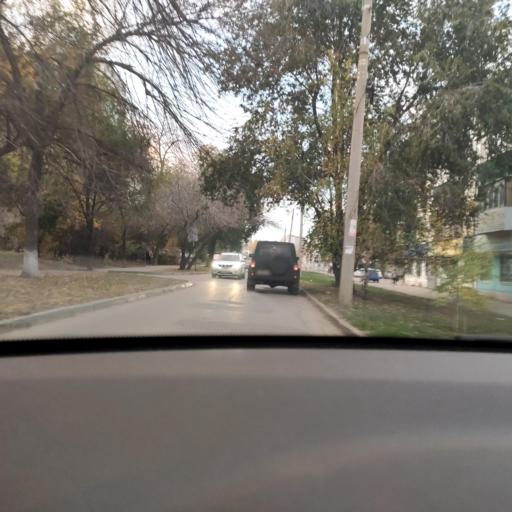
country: RU
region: Samara
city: Samara
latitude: 53.1962
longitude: 50.2041
